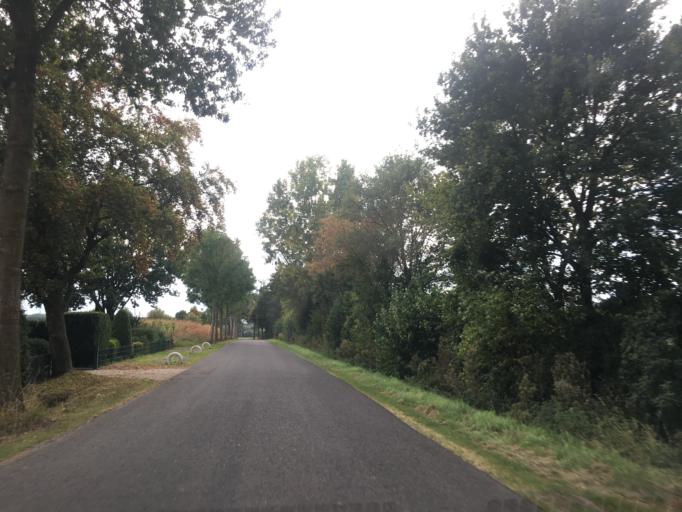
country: DE
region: North Rhine-Westphalia
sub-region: Regierungsbezirk Munster
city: Muenster
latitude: 51.9777
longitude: 7.5412
